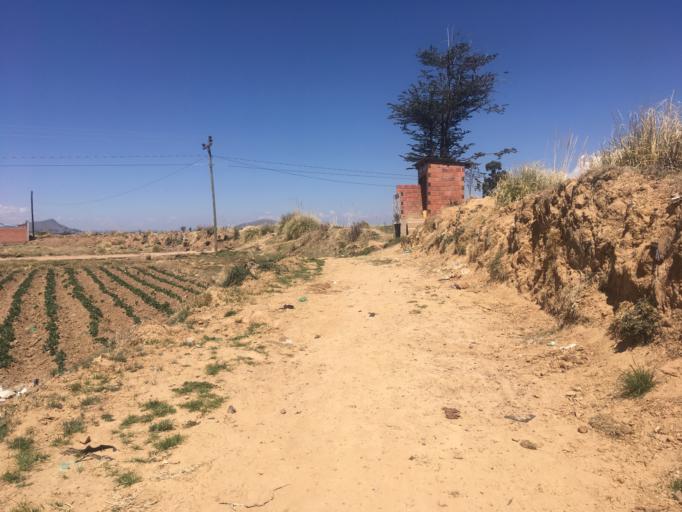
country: BO
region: La Paz
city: Huatajata
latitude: -16.1911
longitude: -68.7474
